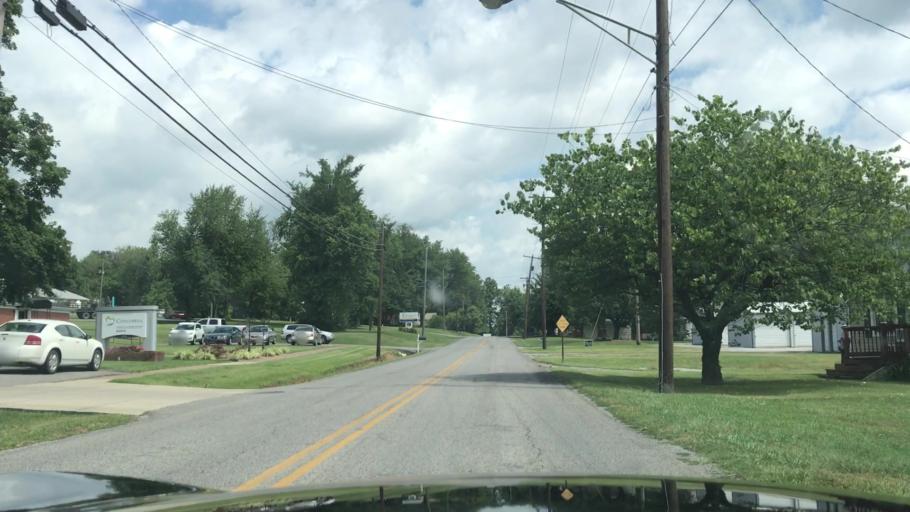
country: US
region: Kentucky
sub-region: Muhlenberg County
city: Greenville
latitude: 37.2159
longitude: -87.1794
